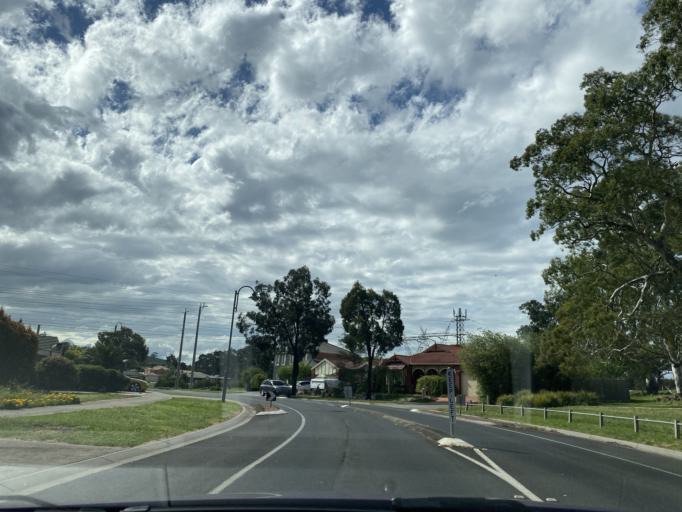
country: AU
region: Victoria
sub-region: Whittlesea
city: Mernda
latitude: -37.6315
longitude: 145.0943
